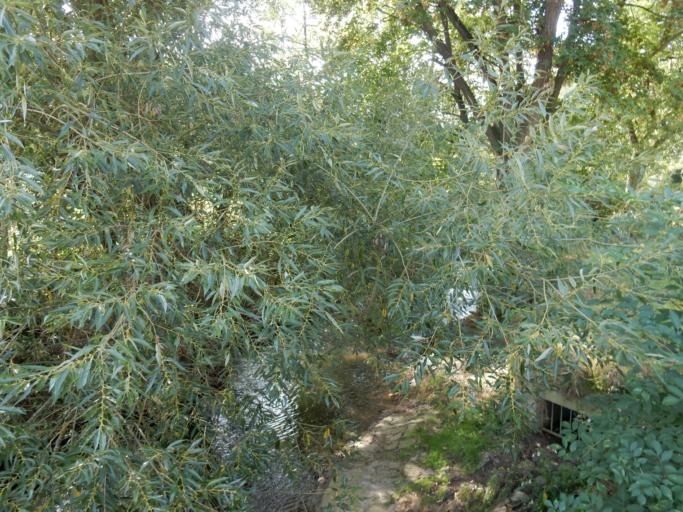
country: LU
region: Luxembourg
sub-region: Canton de Mersch
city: Mersch
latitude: 49.7411
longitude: 6.0977
